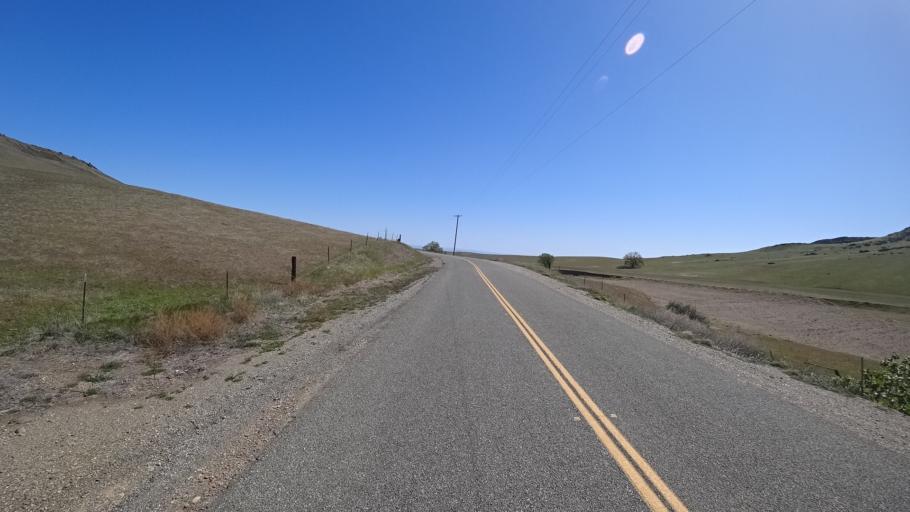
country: US
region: California
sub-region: Glenn County
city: Orland
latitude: 39.7629
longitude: -122.3374
